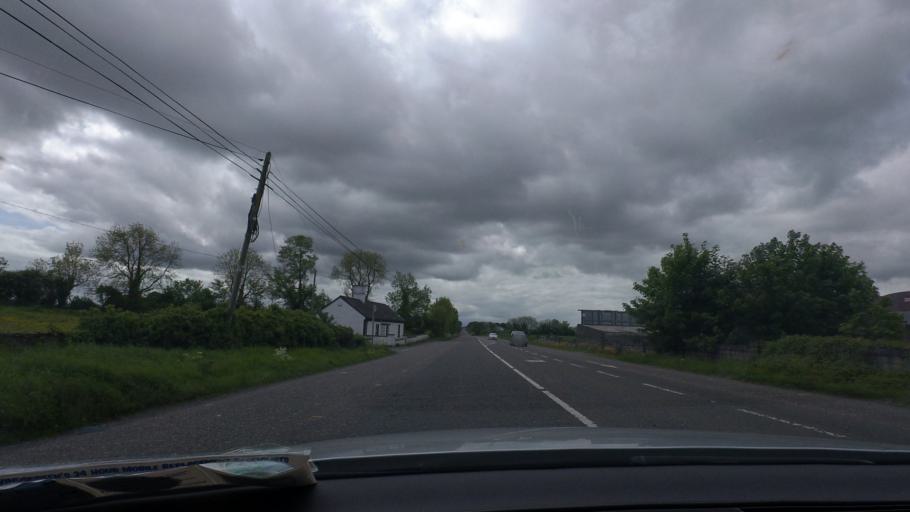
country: IE
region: Munster
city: Thurles
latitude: 52.6287
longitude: -7.7562
